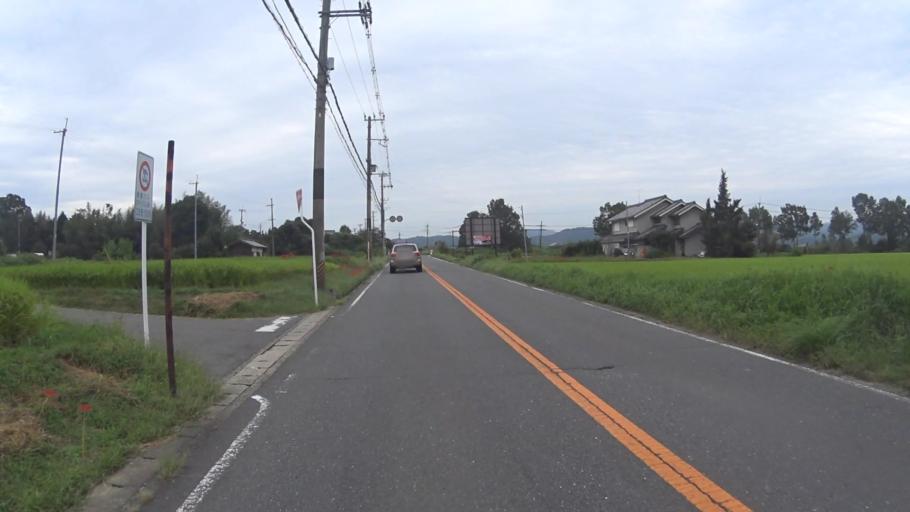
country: JP
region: Nara
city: Nara-shi
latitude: 34.7640
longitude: 135.8570
